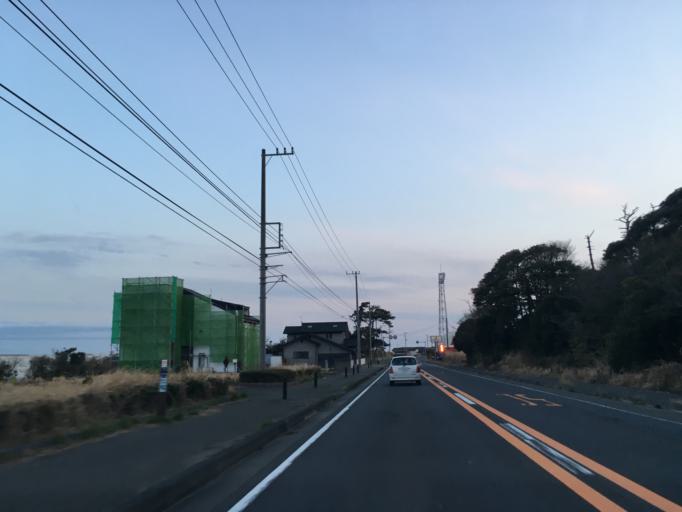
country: JP
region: Ibaraki
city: Kitaibaraki
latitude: 36.7618
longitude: 140.7370
